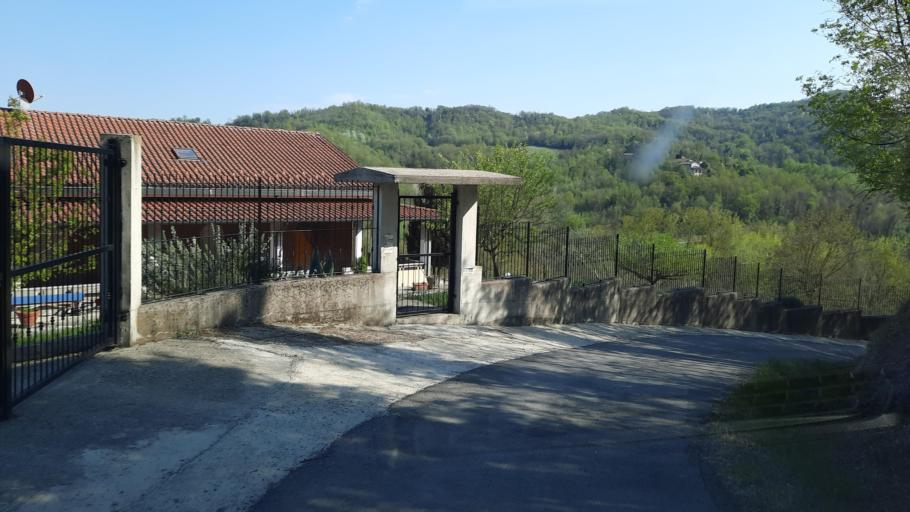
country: IT
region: Piedmont
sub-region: Provincia di Alessandria
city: Villamiroglio
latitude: 45.1346
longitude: 8.1766
